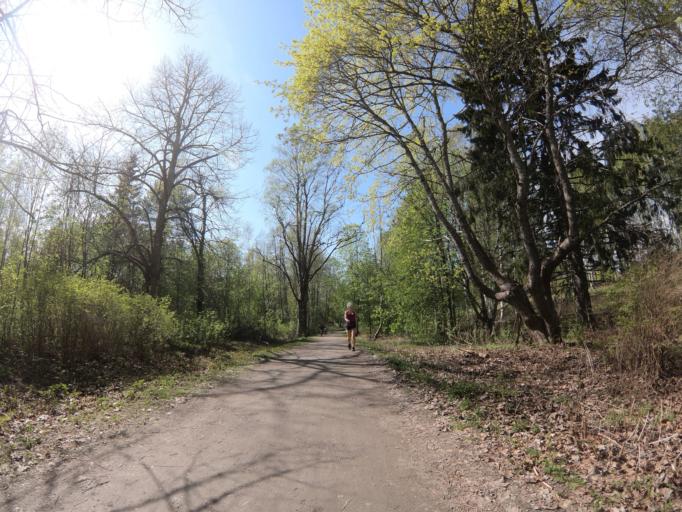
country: SE
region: Vaesterbotten
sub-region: Umea Kommun
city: Roback
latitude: 63.8295
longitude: 20.1769
